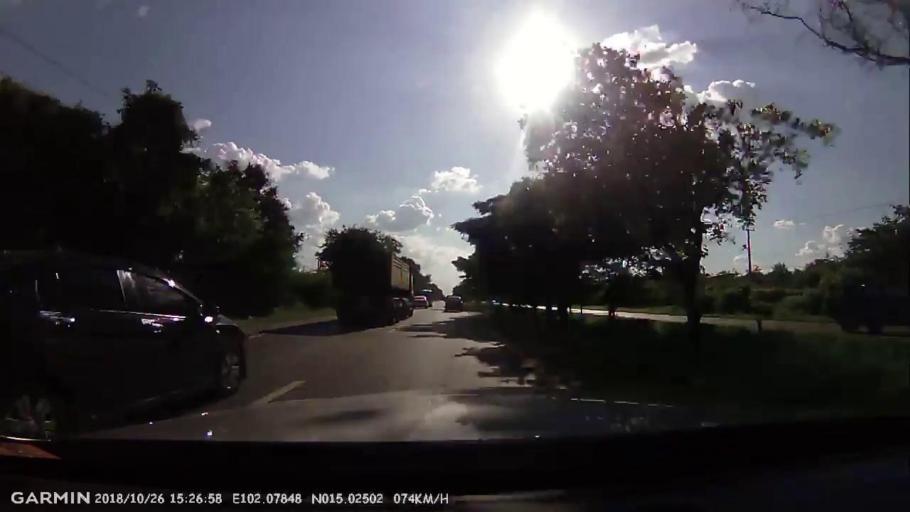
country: TH
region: Nakhon Ratchasima
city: Nakhon Ratchasima
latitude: 15.0249
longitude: 102.0784
